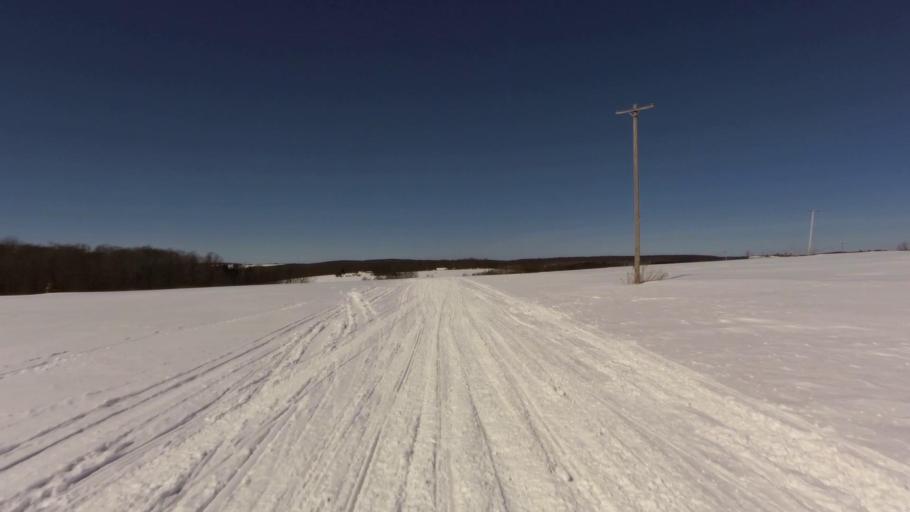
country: US
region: New York
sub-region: Allegany County
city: Houghton
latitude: 42.4214
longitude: -78.3087
